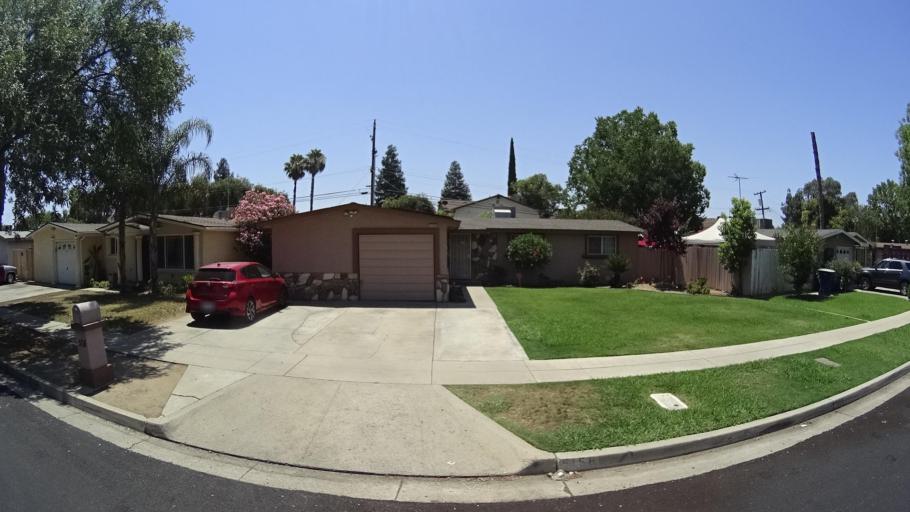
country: US
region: California
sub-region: Fresno County
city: Sunnyside
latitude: 36.7604
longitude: -119.7202
